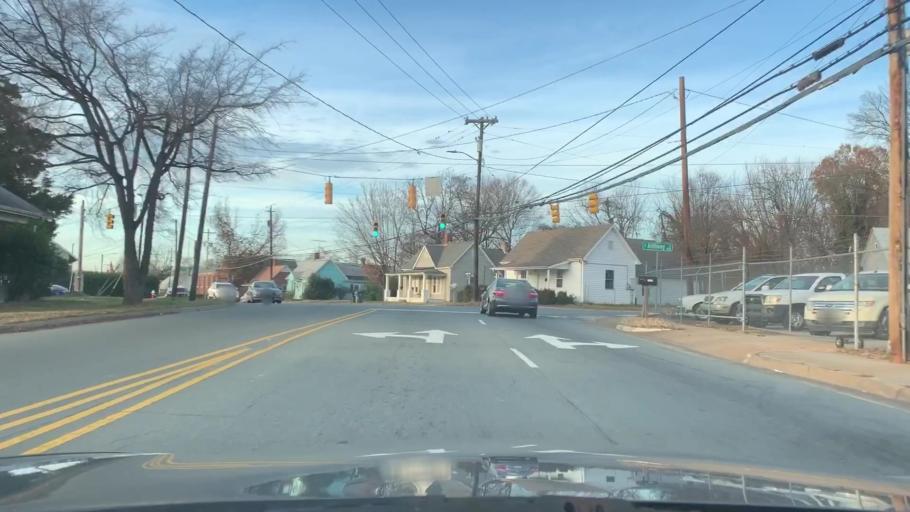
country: US
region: North Carolina
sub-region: Alamance County
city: Burlington
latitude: 36.0827
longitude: -79.4292
